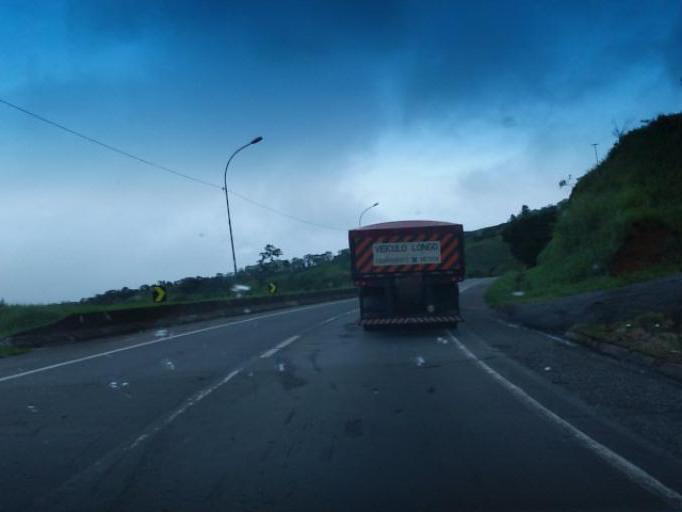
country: BR
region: Sao Paulo
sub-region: Cajati
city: Cajati
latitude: -24.8318
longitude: -48.2139
